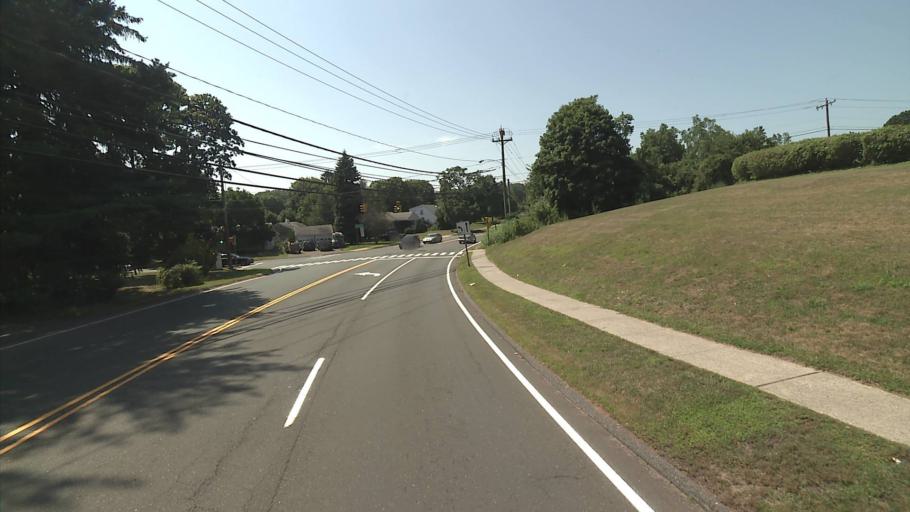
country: US
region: Connecticut
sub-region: New Haven County
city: Branford Center
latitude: 41.2726
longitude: -72.8298
